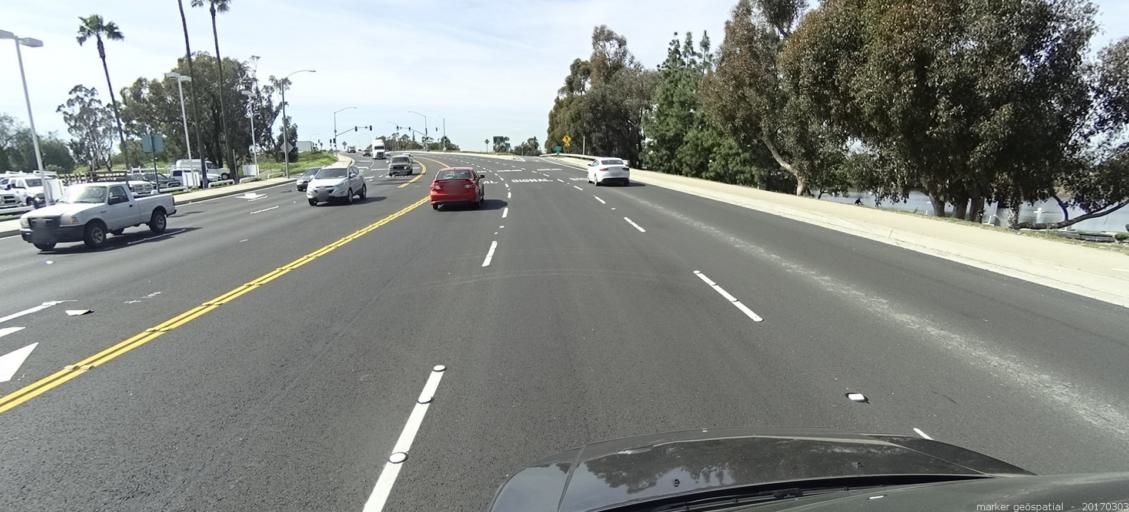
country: US
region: California
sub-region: Orange County
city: Orange
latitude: 33.8178
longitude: -117.8726
